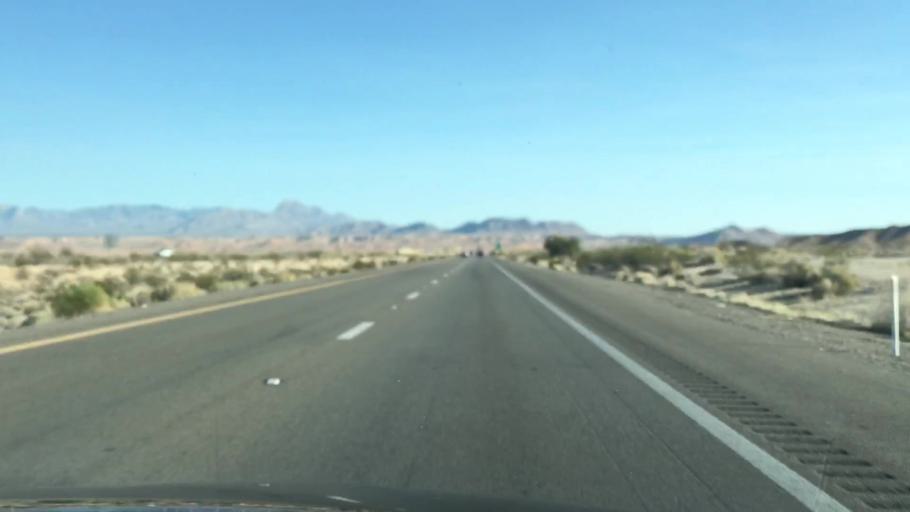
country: US
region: Nevada
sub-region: Clark County
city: Moapa Town
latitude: 36.6439
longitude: -114.5914
